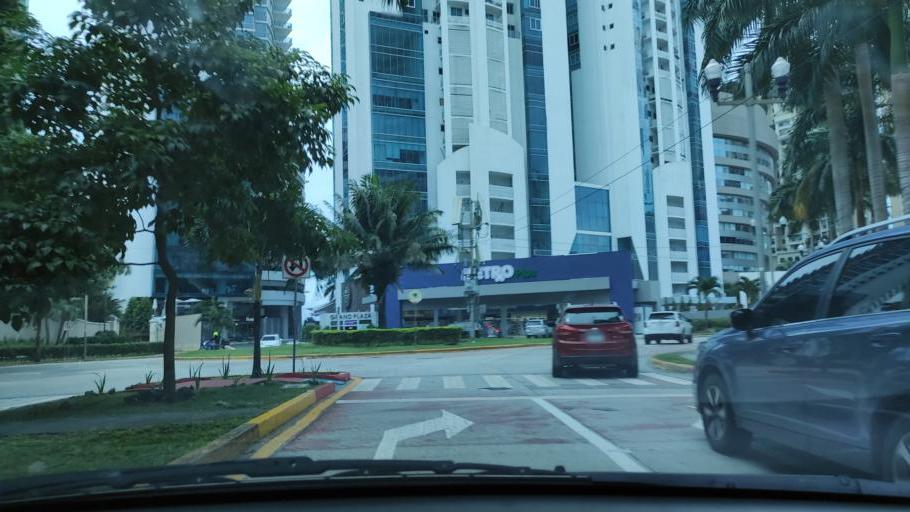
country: PA
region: Panama
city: Panama
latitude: 8.9766
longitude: -79.5083
